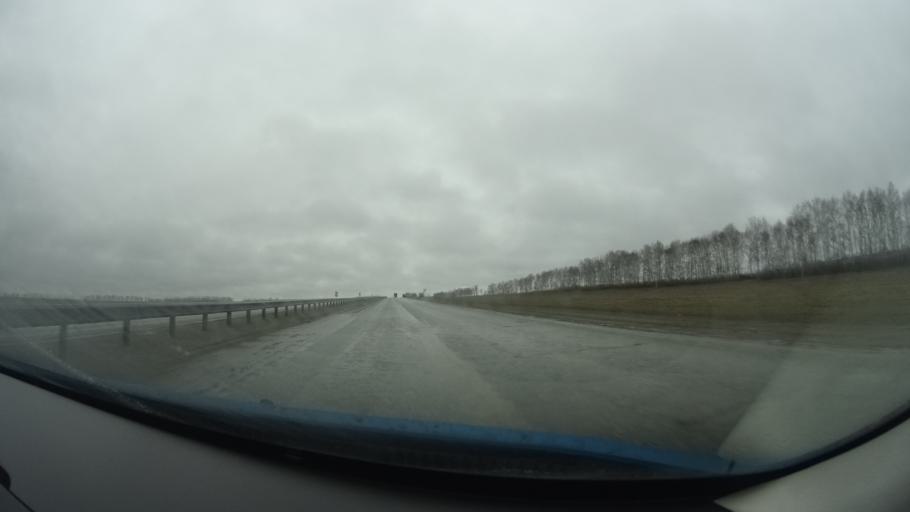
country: RU
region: Bashkortostan
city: Dmitriyevka
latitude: 54.6883
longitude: 55.3046
